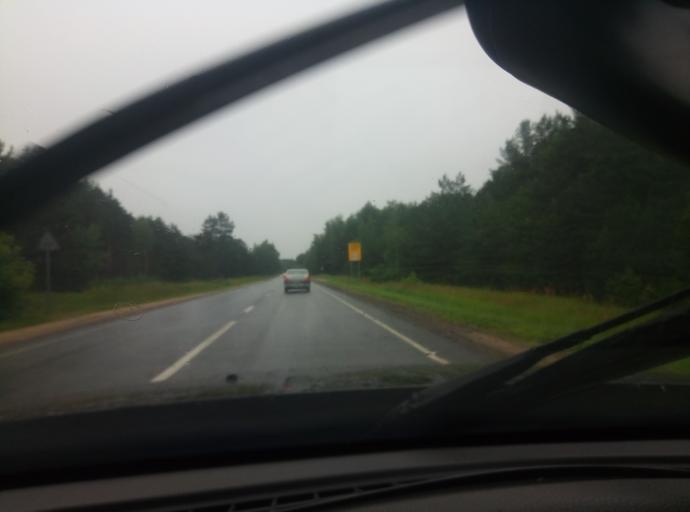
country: RU
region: Moskovskaya
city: Protvino
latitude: 54.8804
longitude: 37.2607
